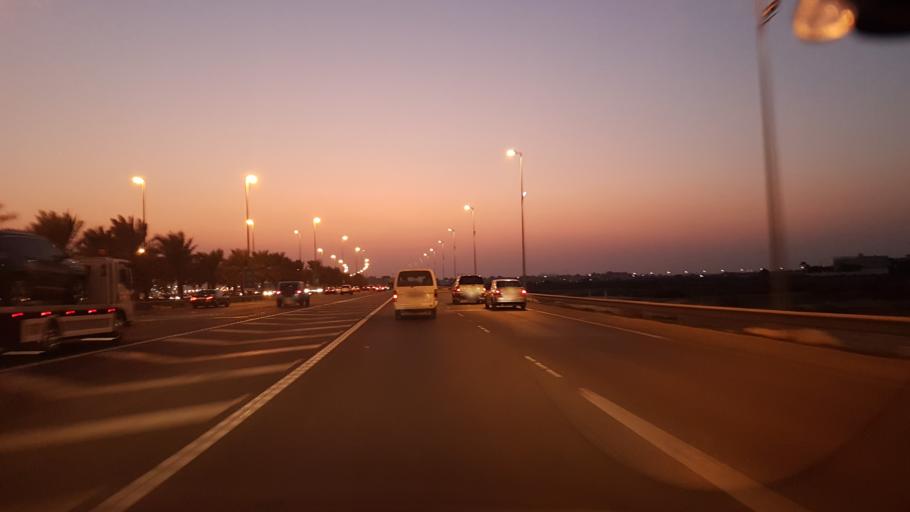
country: BH
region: Northern
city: Madinat `Isa
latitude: 26.1955
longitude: 50.5299
